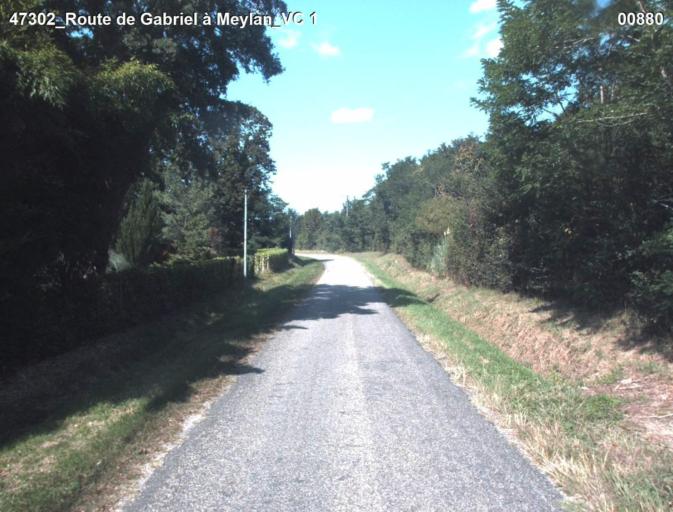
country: FR
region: Aquitaine
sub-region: Departement du Lot-et-Garonne
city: Mezin
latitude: 44.0597
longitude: 0.1439
